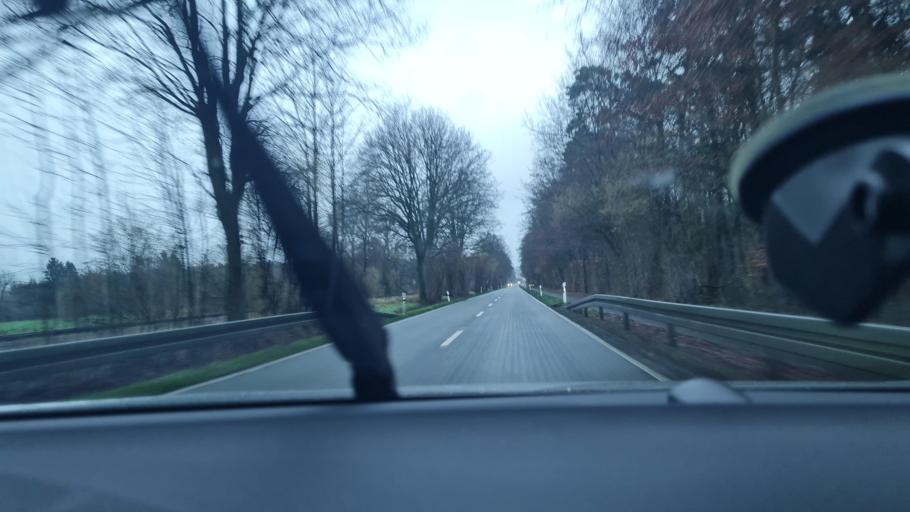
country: DE
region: North Rhine-Westphalia
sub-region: Regierungsbezirk Munster
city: Heiden
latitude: 51.8071
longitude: 6.9071
